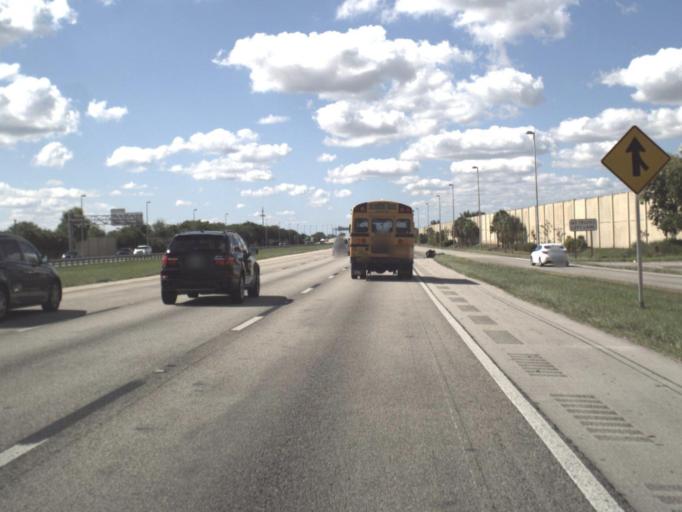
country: US
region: Florida
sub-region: Broward County
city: Parkland
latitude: 26.3022
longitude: -80.2556
